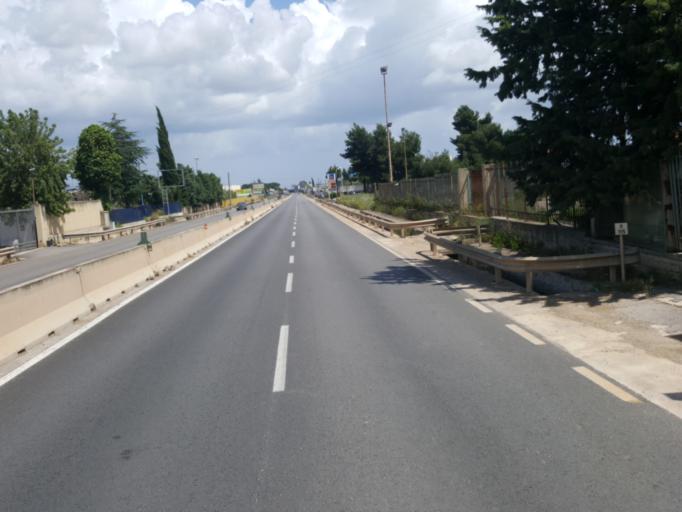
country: IT
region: Apulia
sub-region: Provincia di Bari
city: Bitetto
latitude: 41.0769
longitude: 16.7577
